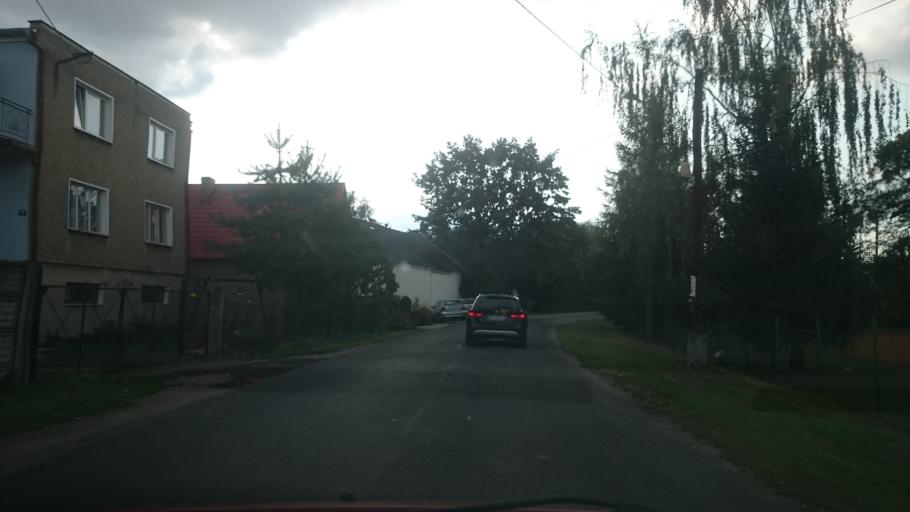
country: PL
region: Opole Voivodeship
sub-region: Powiat nyski
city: Otmuchow
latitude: 50.4994
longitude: 17.2173
